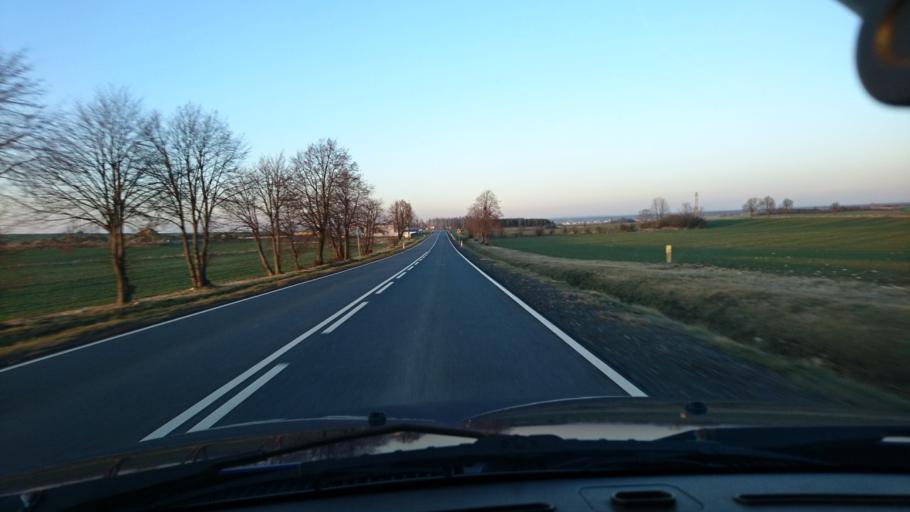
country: PL
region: Silesian Voivodeship
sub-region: Powiat gliwicki
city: Wielowies
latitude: 50.4879
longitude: 18.6056
